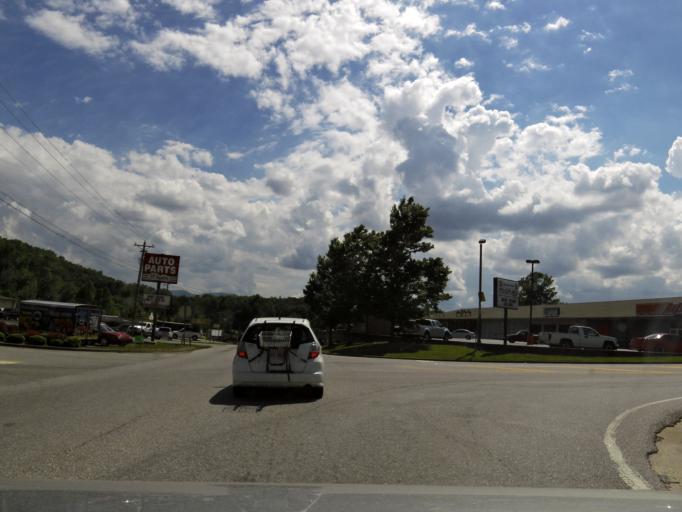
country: US
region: Georgia
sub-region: Union County
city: Blairsville
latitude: 34.8713
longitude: -83.9634
